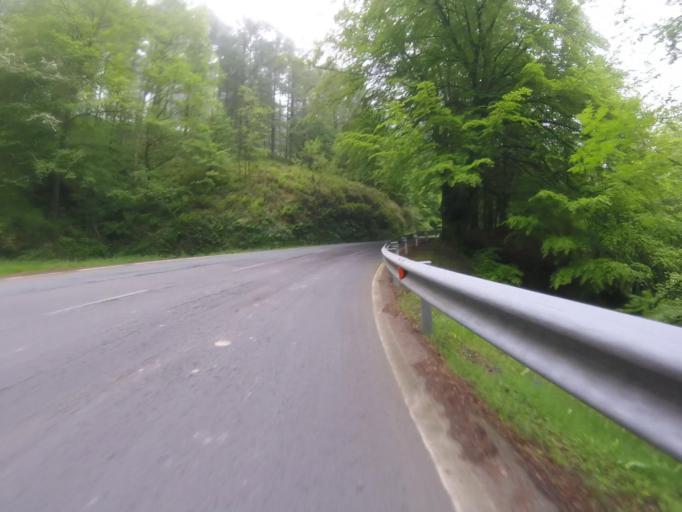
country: ES
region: Navarre
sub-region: Provincia de Navarra
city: Zugarramurdi
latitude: 43.2399
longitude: -1.4837
